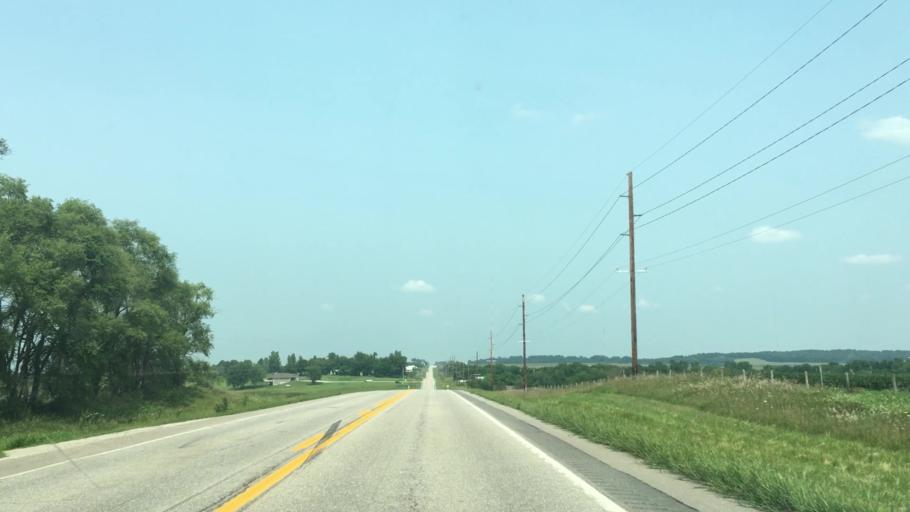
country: US
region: Iowa
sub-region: Benton County
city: Urbana
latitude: 42.2562
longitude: -91.8907
